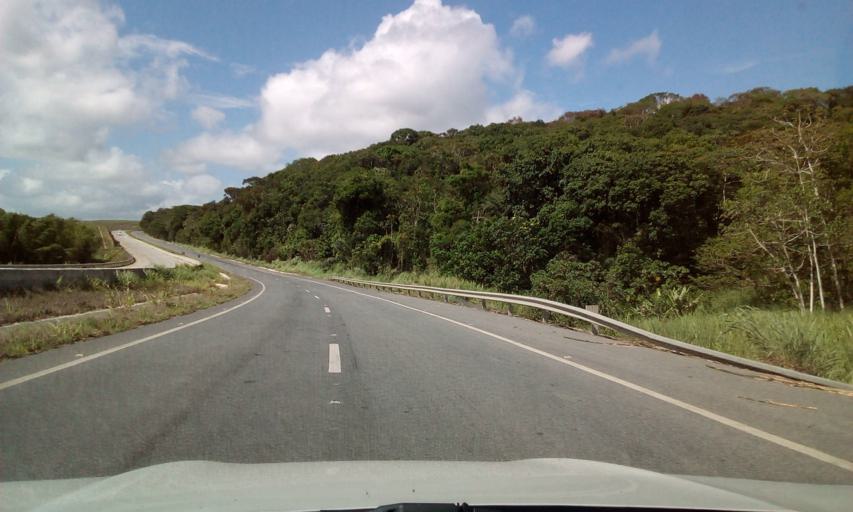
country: BR
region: Alagoas
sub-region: Rio Largo
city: Rio Largo
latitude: -9.4684
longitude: -35.8789
